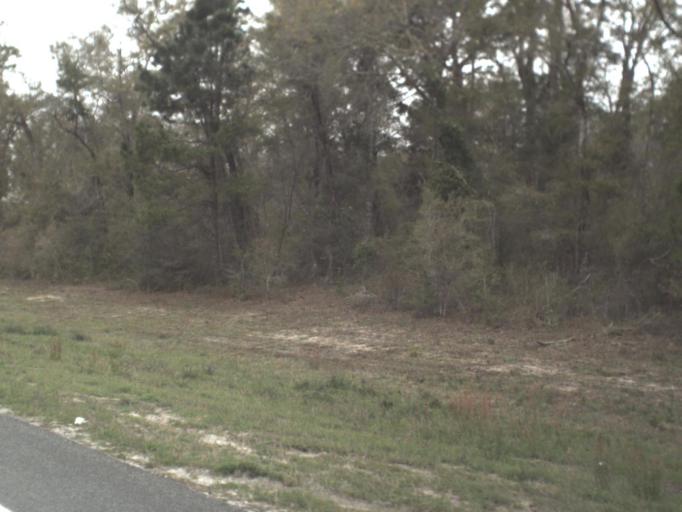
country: US
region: Florida
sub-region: Wakulla County
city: Crawfordville
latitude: 30.1208
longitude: -84.3697
